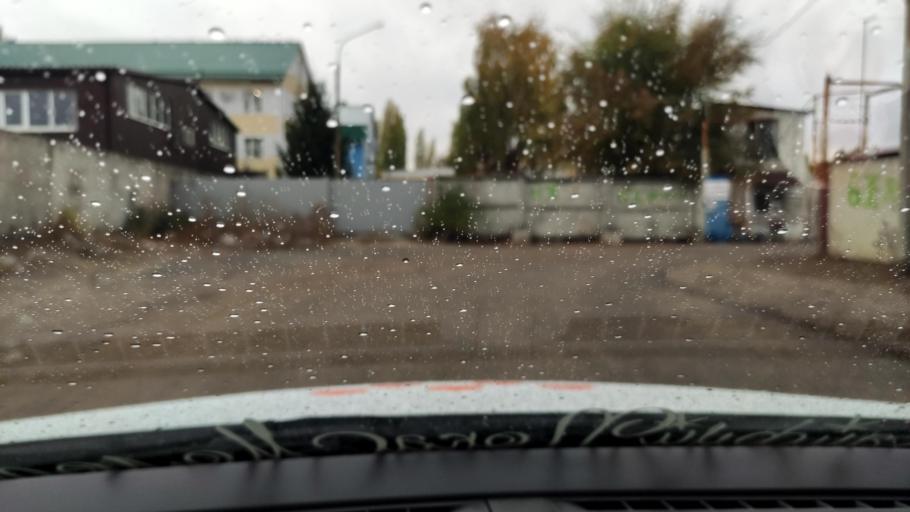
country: RU
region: Voronezj
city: Voronezh
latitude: 51.6616
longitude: 39.1481
